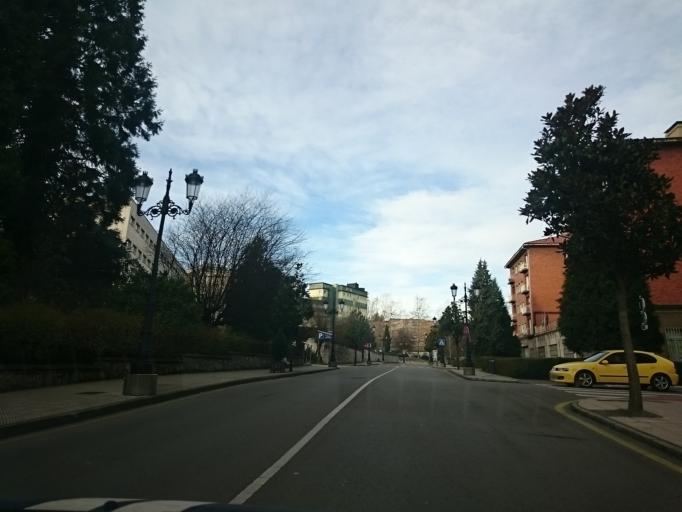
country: ES
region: Asturias
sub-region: Province of Asturias
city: Oviedo
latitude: 43.3590
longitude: -5.8633
